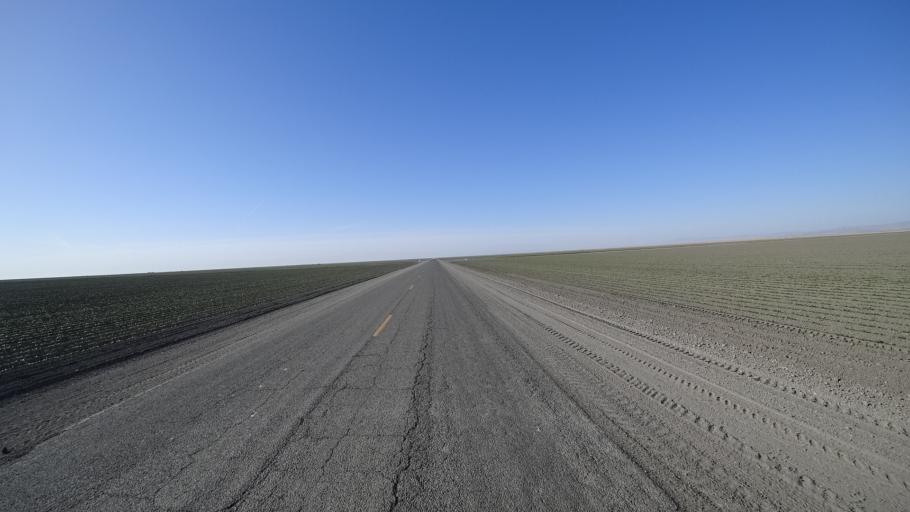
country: US
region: California
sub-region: Kings County
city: Stratford
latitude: 36.0964
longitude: -119.7979
